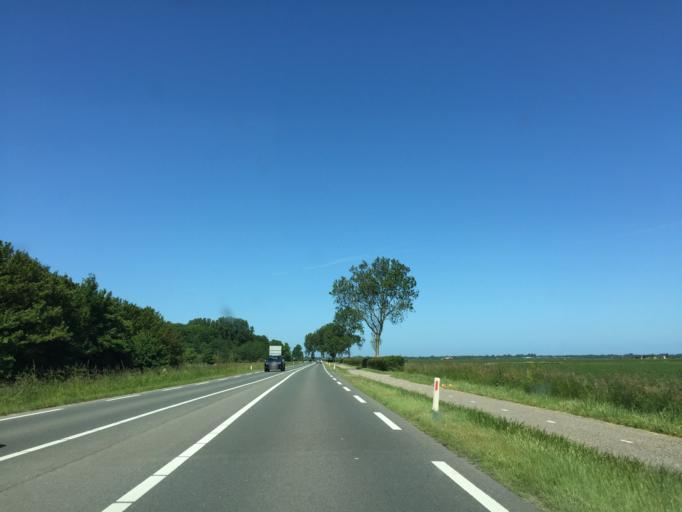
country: NL
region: Zeeland
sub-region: Schouwen-Duiveland
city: Renesse
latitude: 51.7012
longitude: 3.8046
